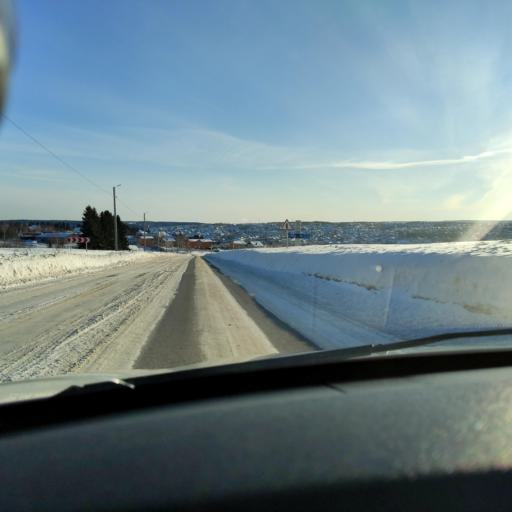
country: RU
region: Perm
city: Polazna
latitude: 58.3141
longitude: 56.4302
